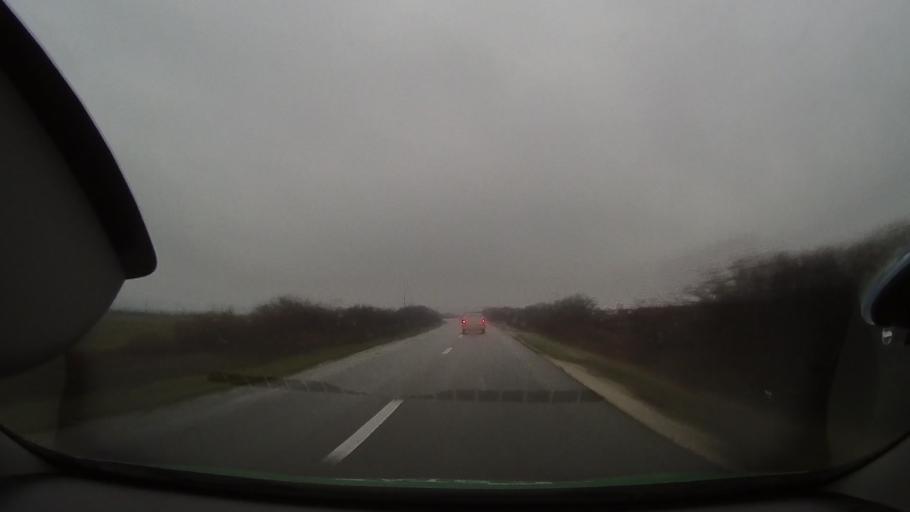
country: RO
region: Arad
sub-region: Comuna Craiova
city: Craiova
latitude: 46.5458
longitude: 21.9599
